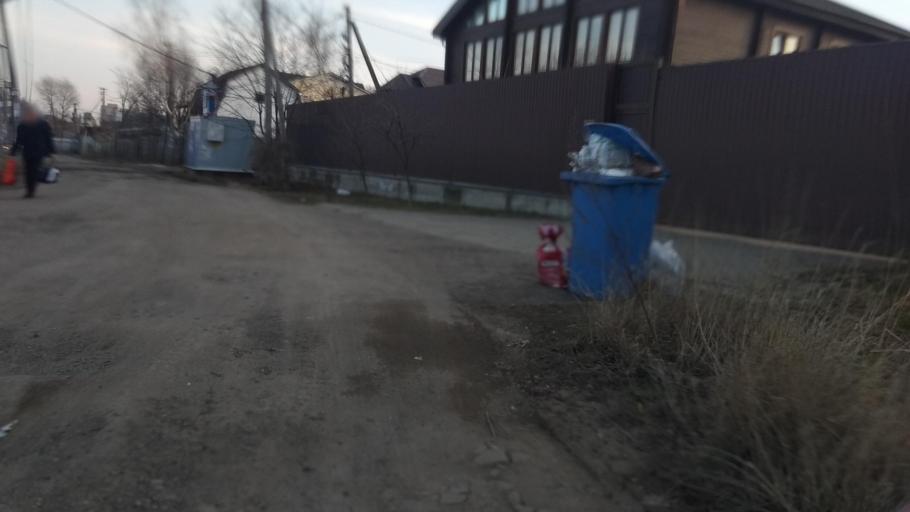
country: RU
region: Moskovskaya
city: Razvilka
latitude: 55.5745
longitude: 37.7533
